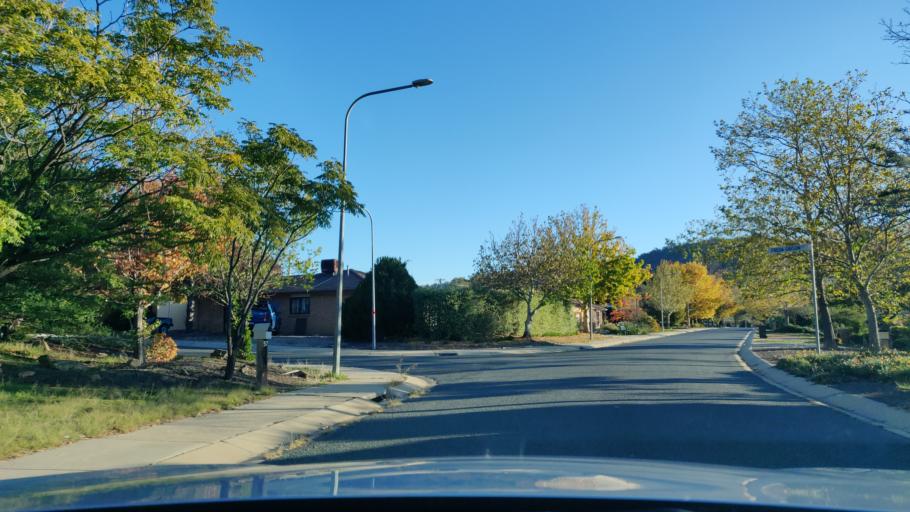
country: AU
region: Australian Capital Territory
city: Macarthur
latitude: -35.4450
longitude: 149.1265
